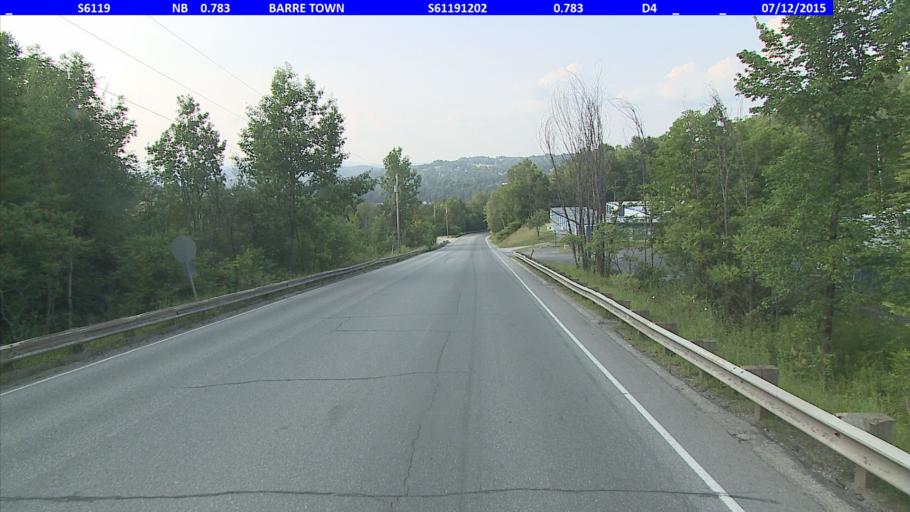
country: US
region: Vermont
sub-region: Washington County
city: South Barre
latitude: 44.1783
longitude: -72.4958
